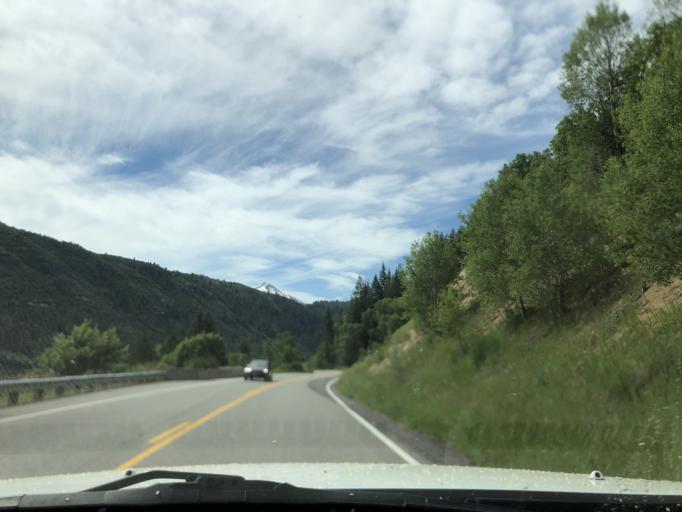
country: US
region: Colorado
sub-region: Delta County
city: Paonia
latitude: 38.9740
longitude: -107.3420
